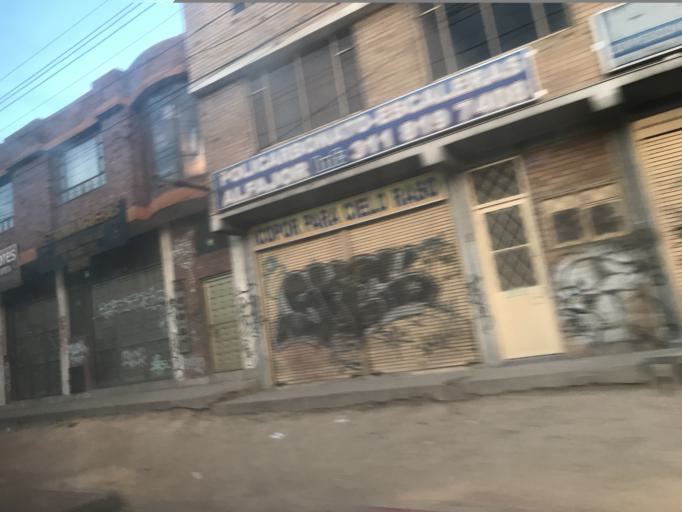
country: CO
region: Cundinamarca
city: Soacha
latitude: 4.5819
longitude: -74.2135
